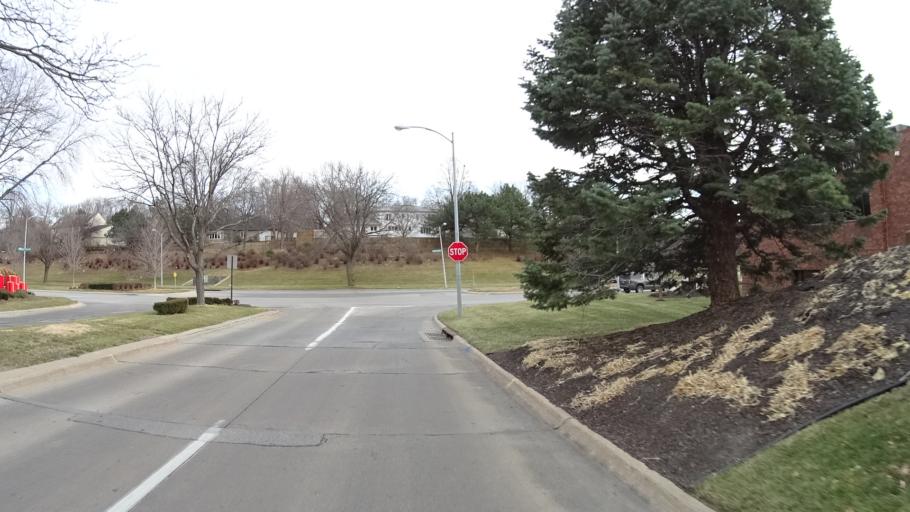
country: US
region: Nebraska
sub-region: Douglas County
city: Ralston
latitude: 41.2582
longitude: -96.0732
